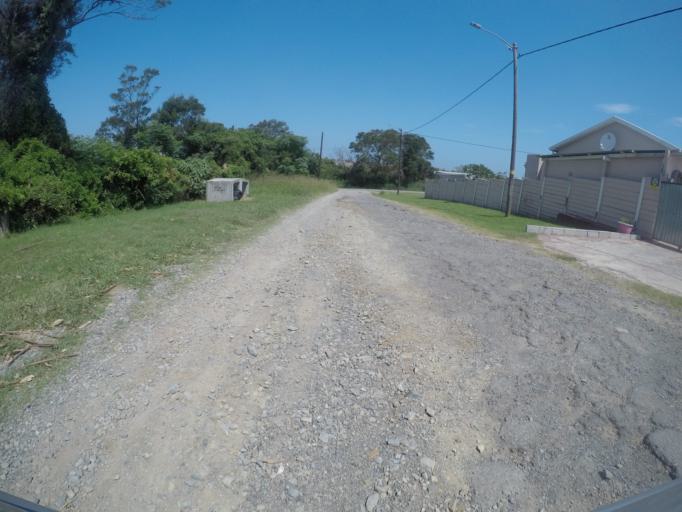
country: ZA
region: Eastern Cape
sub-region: Buffalo City Metropolitan Municipality
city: East London
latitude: -32.9697
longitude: 27.8583
